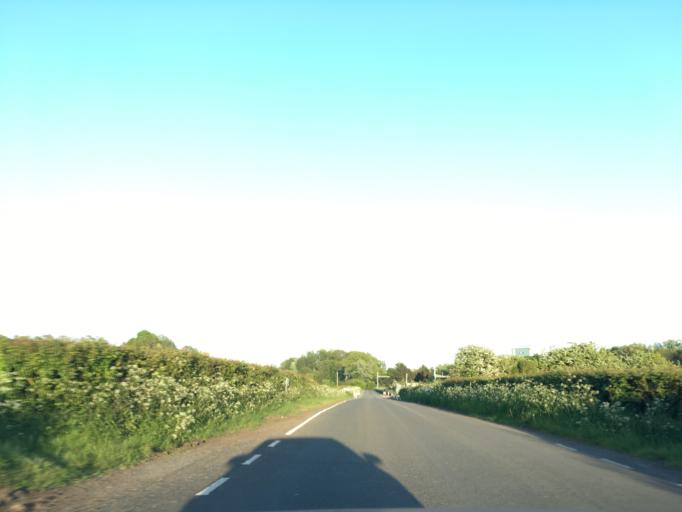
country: GB
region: Wales
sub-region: Newport
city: Bishton
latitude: 51.5820
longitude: -2.8925
